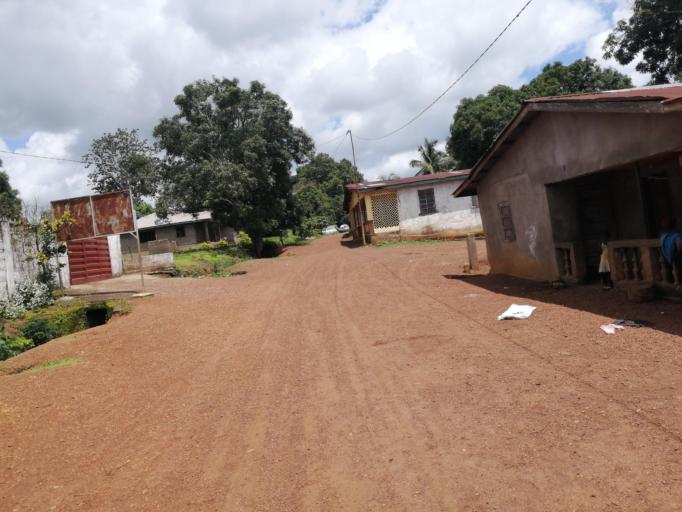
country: SL
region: Northern Province
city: Port Loko
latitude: 8.7698
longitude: -12.7825
